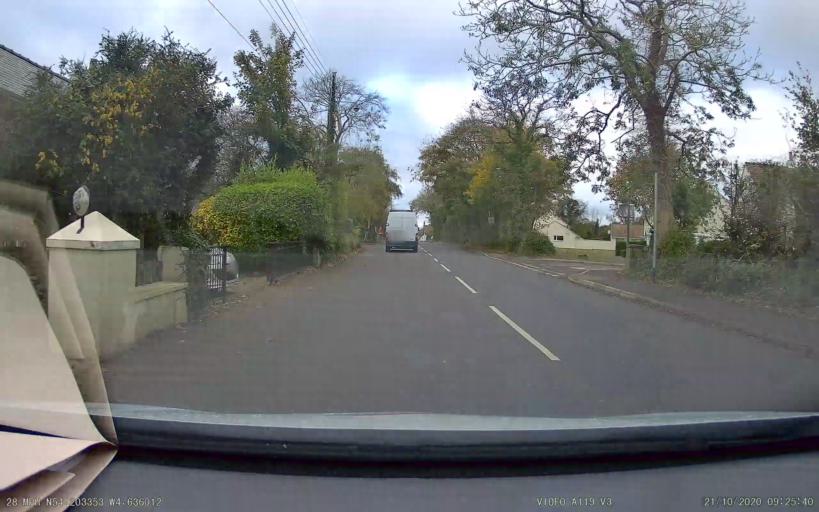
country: IM
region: Castletown
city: Castletown
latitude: 54.0000
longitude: -4.6360
